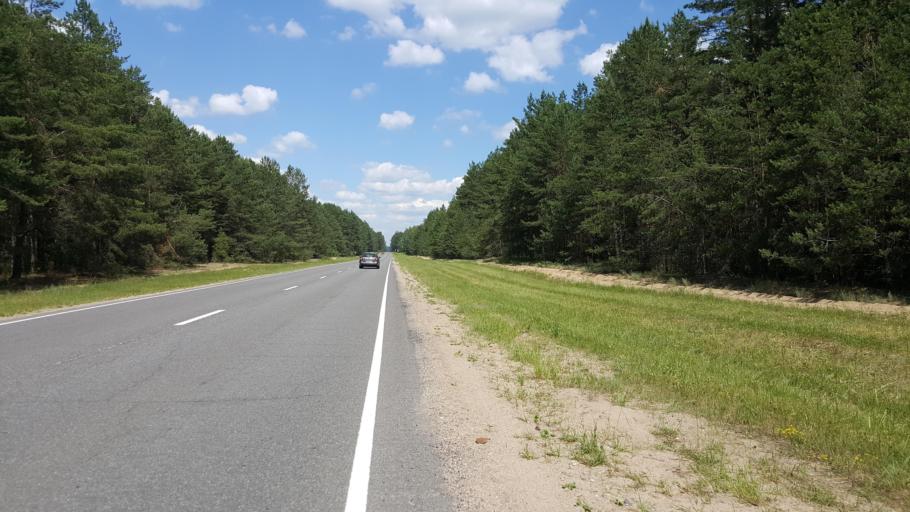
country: BY
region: Brest
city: Kamyanyuki
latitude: 52.5362
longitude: 23.7920
